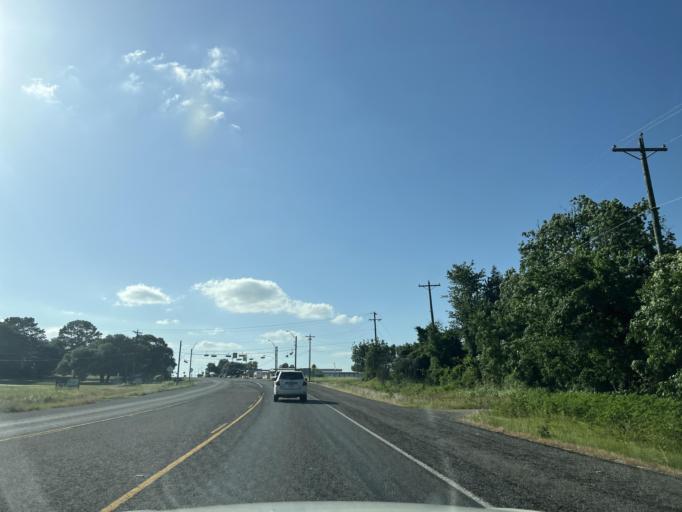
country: US
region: Texas
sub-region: Washington County
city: Brenham
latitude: 30.1556
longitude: -96.3700
